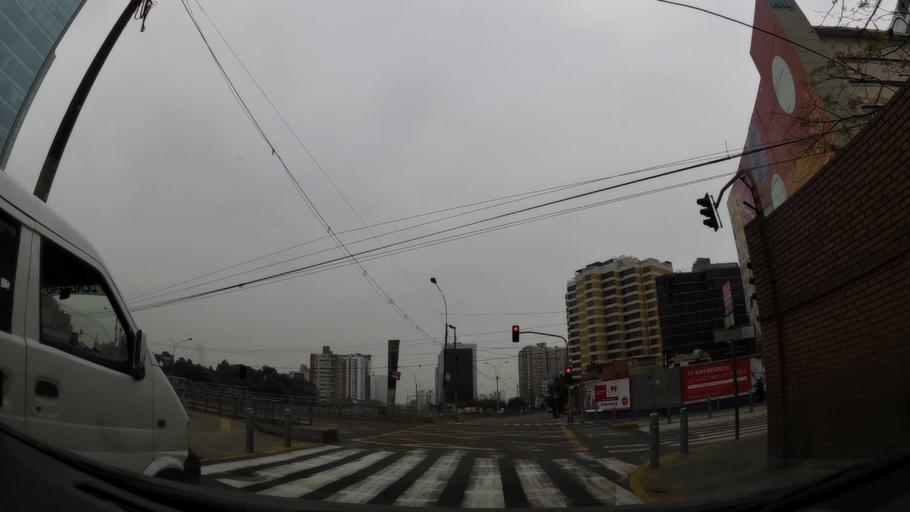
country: PE
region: Lima
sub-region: Lima
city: Surco
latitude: -12.1251
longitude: -77.0245
